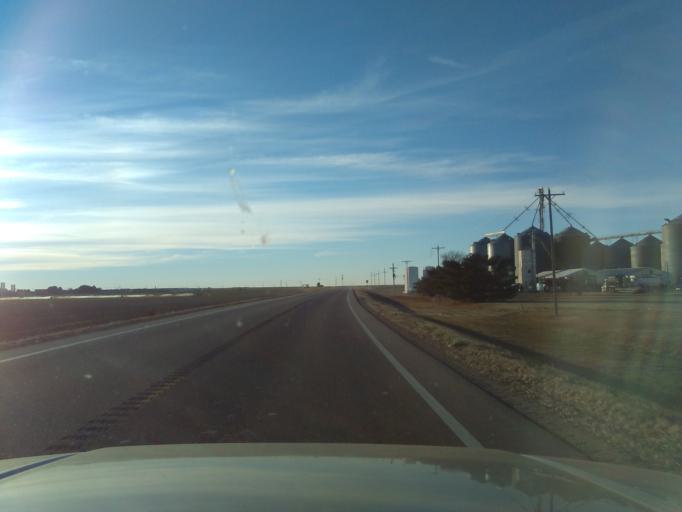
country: US
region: Kansas
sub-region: Thomas County
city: Colby
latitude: 39.4480
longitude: -100.8148
